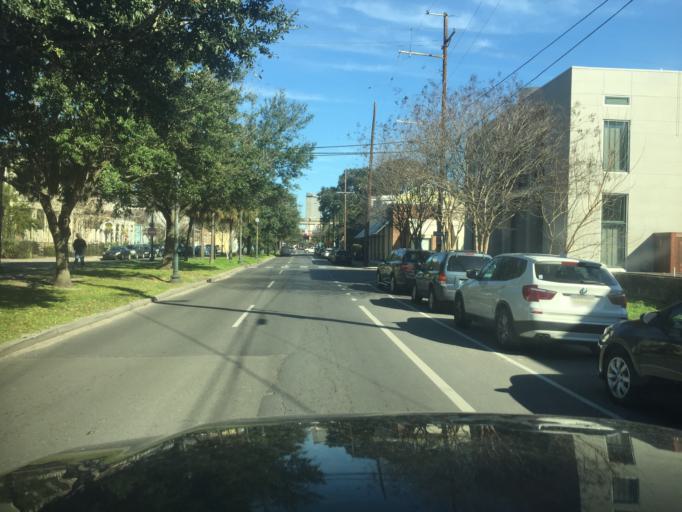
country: US
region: Louisiana
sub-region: Orleans Parish
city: New Orleans
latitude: 29.9381
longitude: -90.0727
